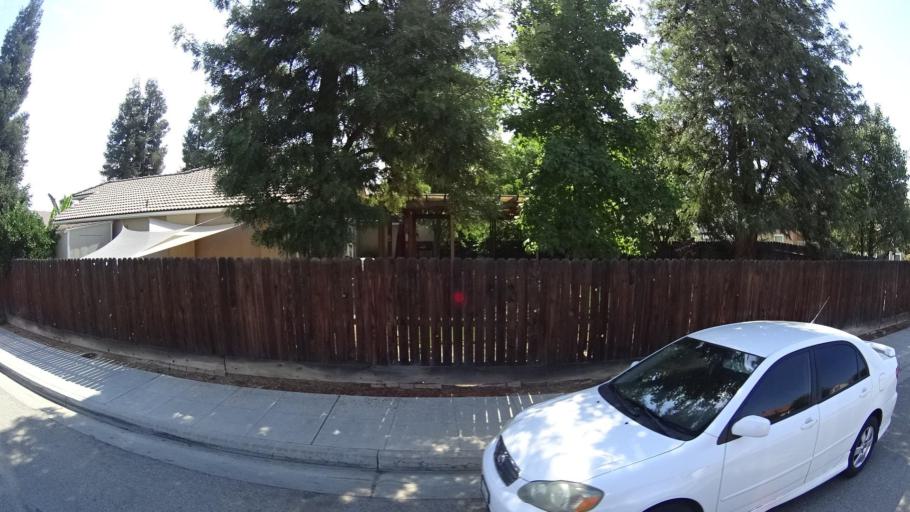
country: US
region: California
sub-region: Fresno County
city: Sunnyside
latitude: 36.7210
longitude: -119.6962
